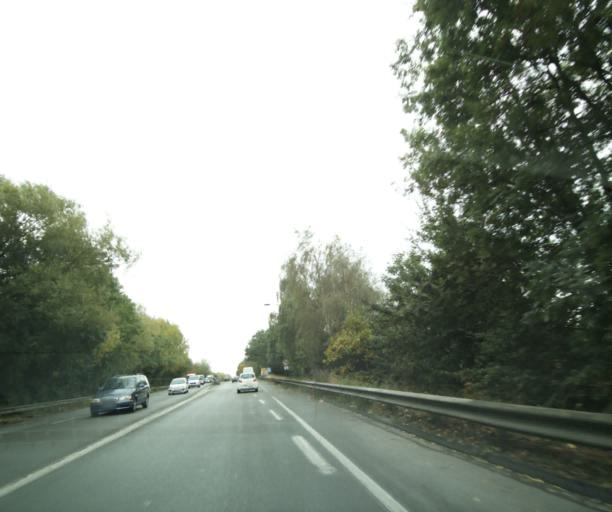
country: FR
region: Nord-Pas-de-Calais
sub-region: Departement du Nord
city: Neuville-en-Ferrain
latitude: 50.7525
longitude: 3.1401
